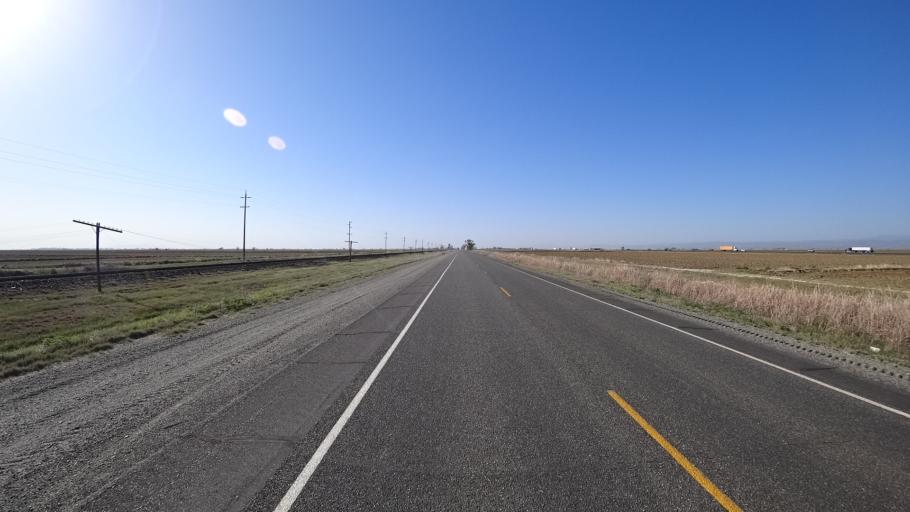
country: US
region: California
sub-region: Glenn County
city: Willows
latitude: 39.4866
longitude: -122.1931
